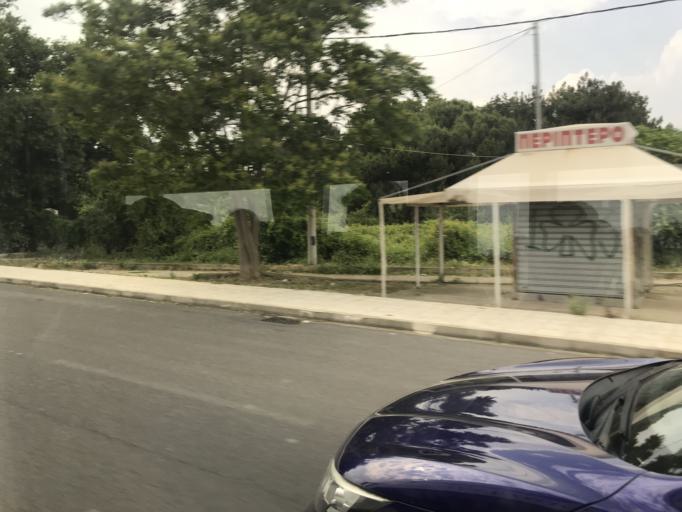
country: GR
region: East Macedonia and Thrace
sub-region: Nomos Evrou
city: Alexandroupoli
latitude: 40.8492
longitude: 25.8956
